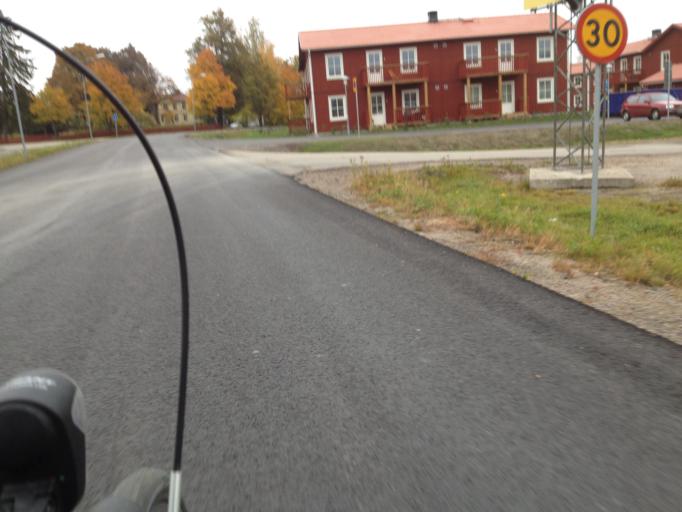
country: SE
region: Gaevleborg
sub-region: Bollnas Kommun
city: Bollnas
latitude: 61.3431
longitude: 16.3857
